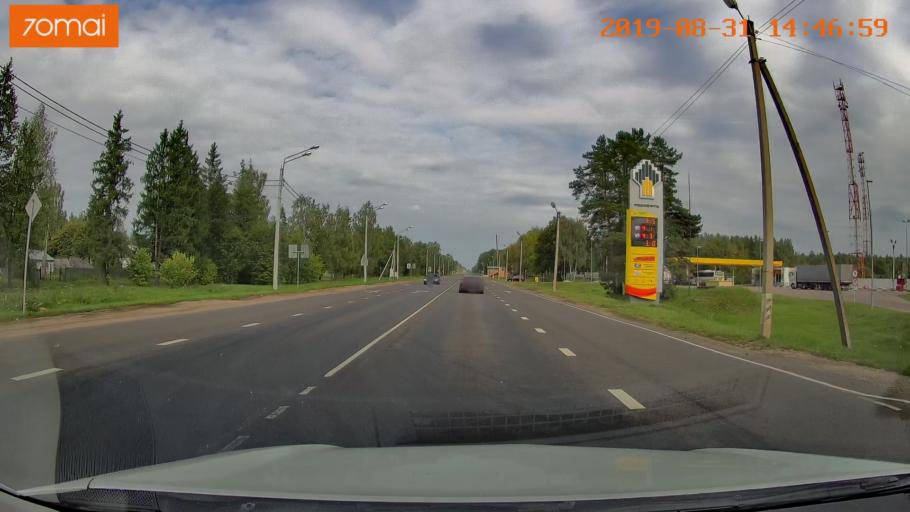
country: RU
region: Kaluga
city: Betlitsa
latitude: 54.2369
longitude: 33.7192
